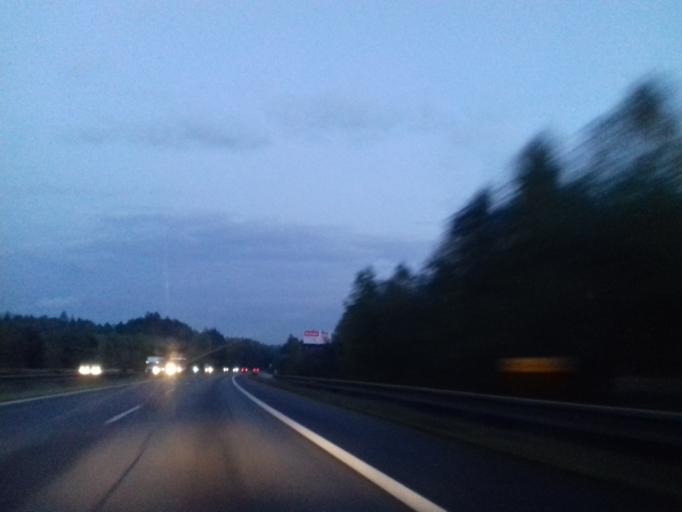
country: CZ
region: Vysocina
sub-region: Okres Pelhrimov
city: Humpolec
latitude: 49.5595
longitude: 15.3154
